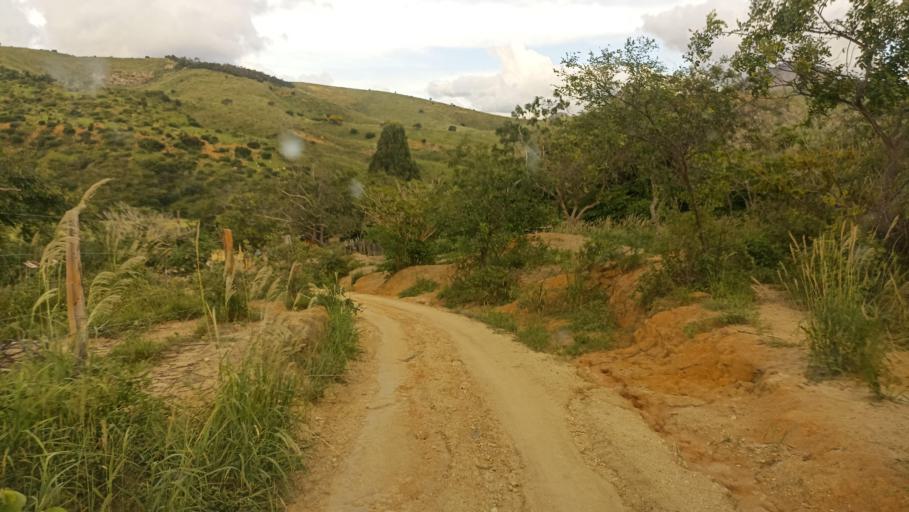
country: BR
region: Minas Gerais
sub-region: Almenara
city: Almenara
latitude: -16.5376
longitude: -40.4423
